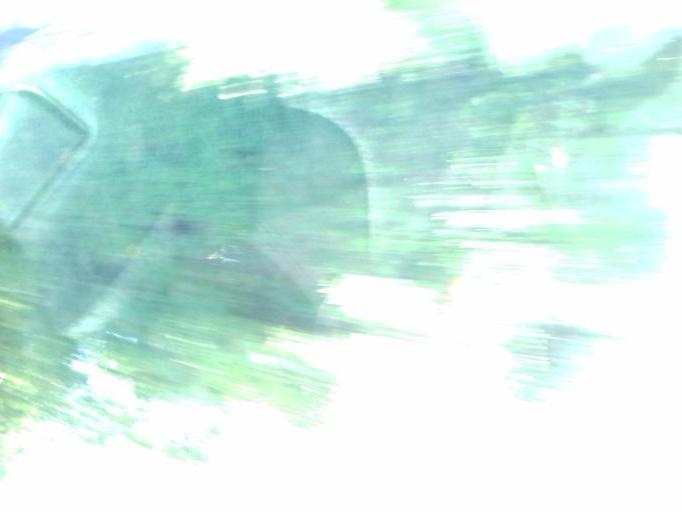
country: IE
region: Leinster
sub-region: Fingal County
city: Swords
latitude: 53.5300
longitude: -6.2692
